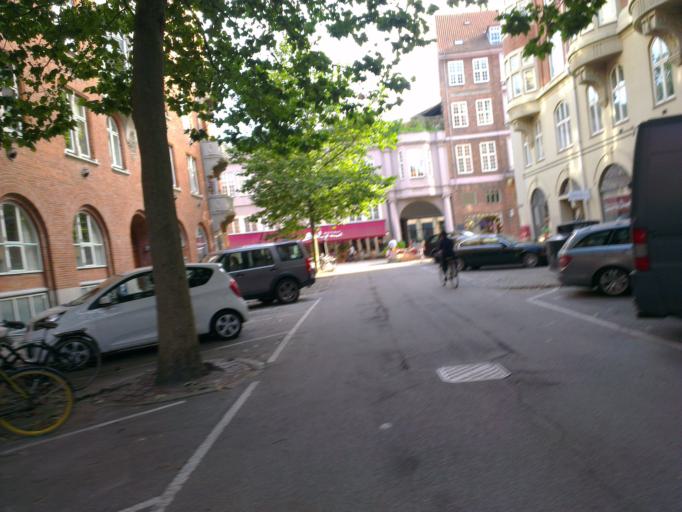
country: DK
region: Capital Region
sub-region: Kobenhavn
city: Christianshavn
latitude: 55.6878
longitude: 12.5911
